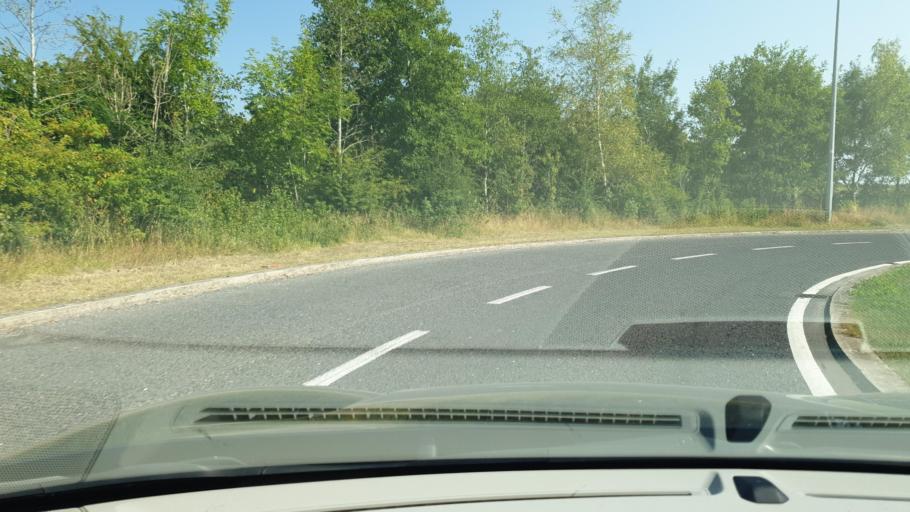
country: IE
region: Leinster
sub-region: An Mhi
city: Dunshaughlin
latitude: 53.5099
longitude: -6.5563
